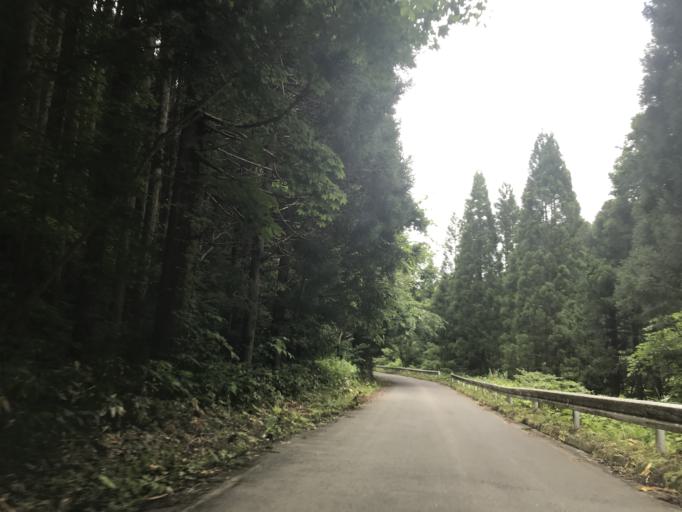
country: JP
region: Iwate
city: Ichinoseki
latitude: 38.9656
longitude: 140.9058
